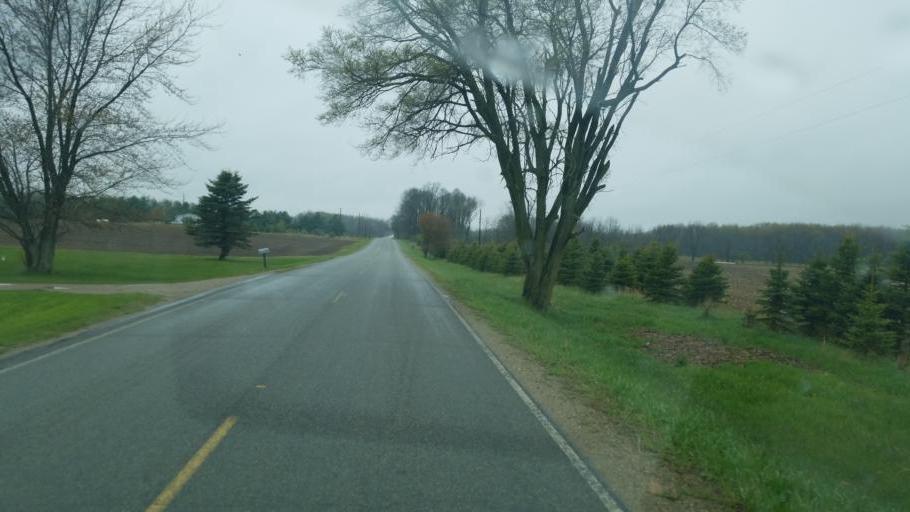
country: US
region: Michigan
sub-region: Montcalm County
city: Lakeview
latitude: 43.4894
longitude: -85.2952
